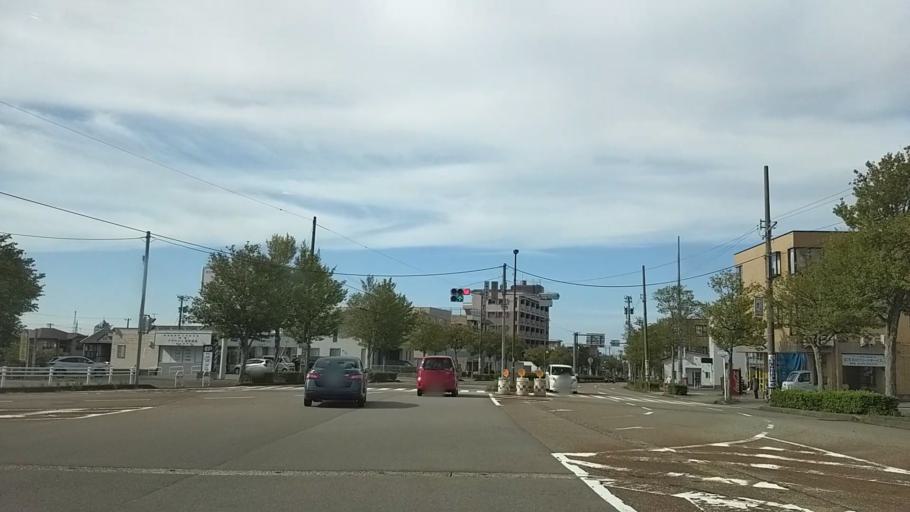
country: JP
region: Ishikawa
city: Nonoichi
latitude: 36.5240
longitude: 136.6395
